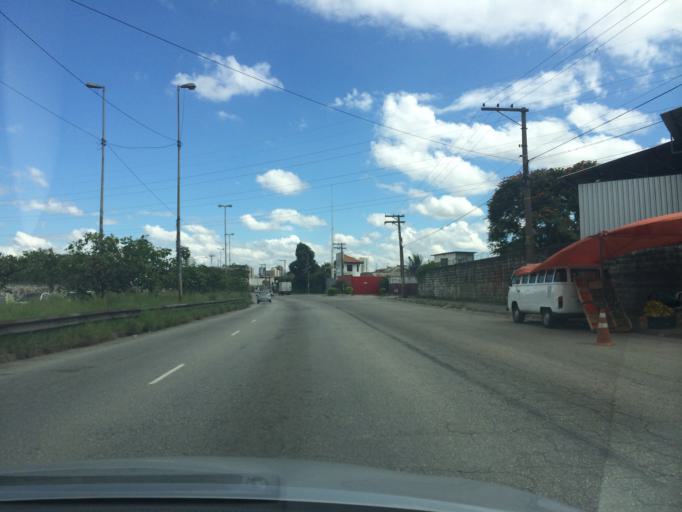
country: BR
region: Sao Paulo
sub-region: Guarulhos
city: Guarulhos
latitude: -23.5146
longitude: -46.5611
